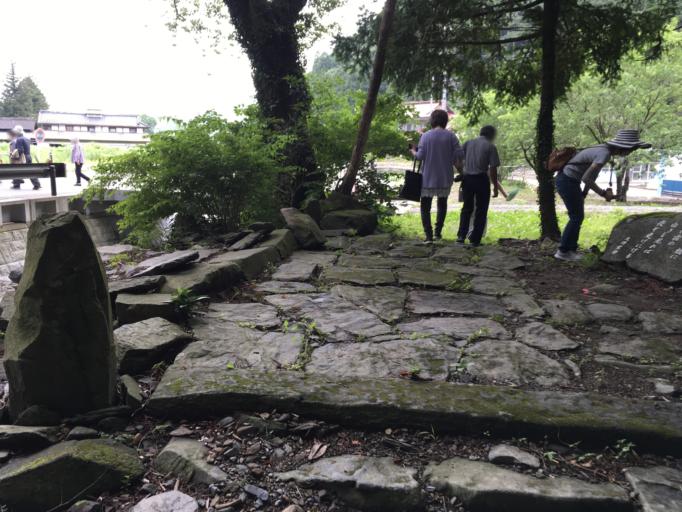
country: JP
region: Miyagi
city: Ishinomaki
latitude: 38.5892
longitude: 141.3117
